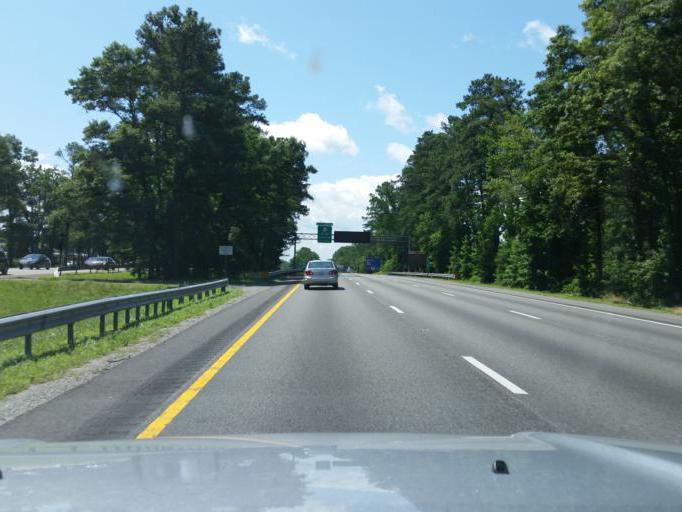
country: US
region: Virginia
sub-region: Hanover County
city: Ashland
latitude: 37.7114
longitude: -77.4481
